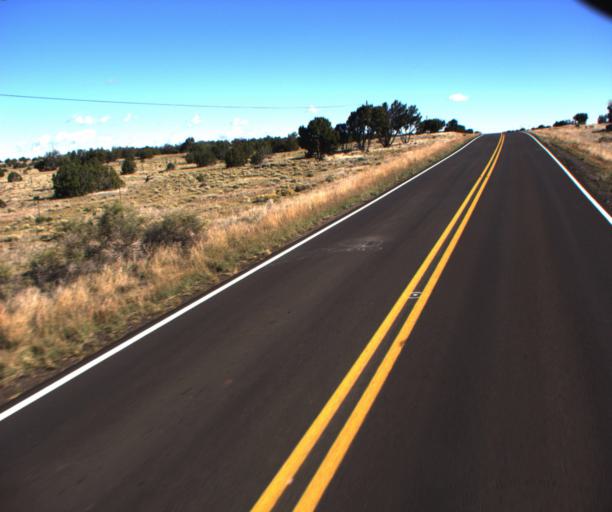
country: US
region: Arizona
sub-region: Apache County
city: Saint Johns
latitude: 34.4011
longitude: -109.6557
